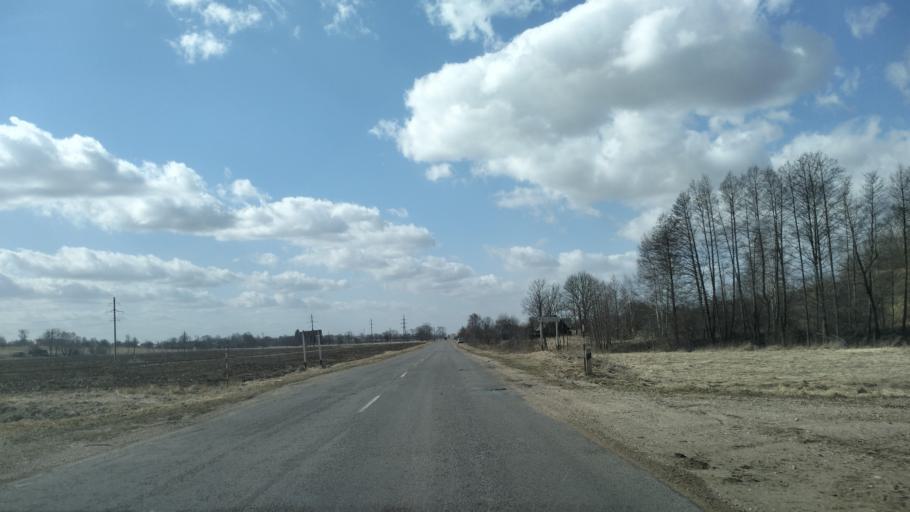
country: BY
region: Grodnenskaya
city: Karelichy
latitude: 53.6605
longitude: 26.1213
